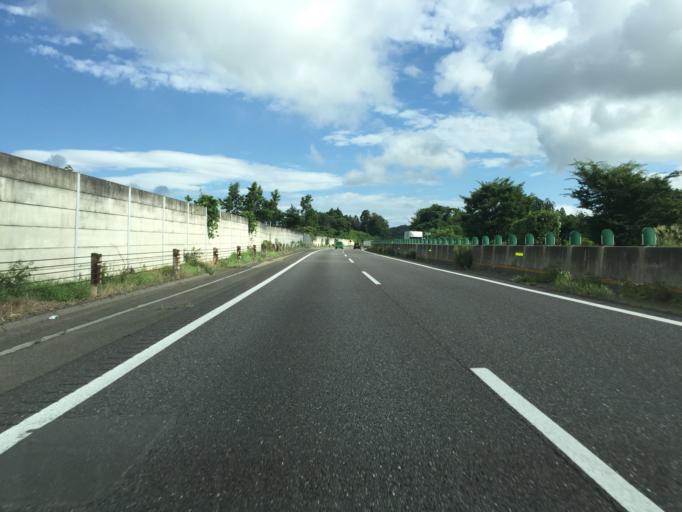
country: JP
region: Fukushima
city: Nihommatsu
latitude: 37.6137
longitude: 140.4230
